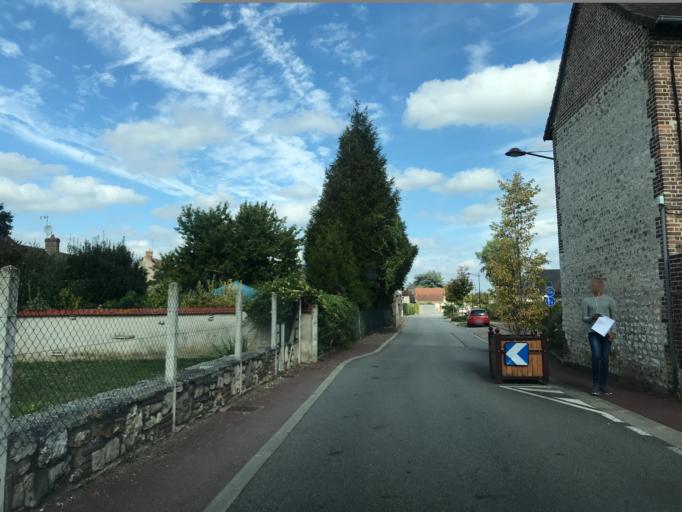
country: FR
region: Haute-Normandie
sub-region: Departement de l'Eure
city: Le Vaudreuil
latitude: 49.2526
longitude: 1.1975
